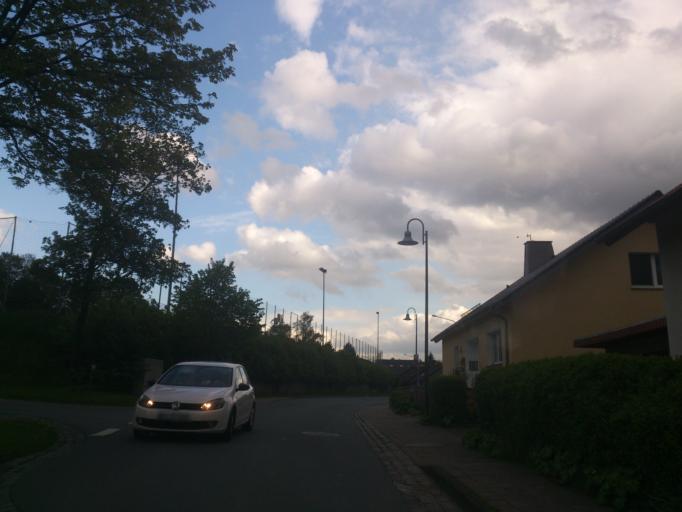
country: DE
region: North Rhine-Westphalia
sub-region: Regierungsbezirk Detmold
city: Altenbeken
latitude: 51.7126
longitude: 8.9397
